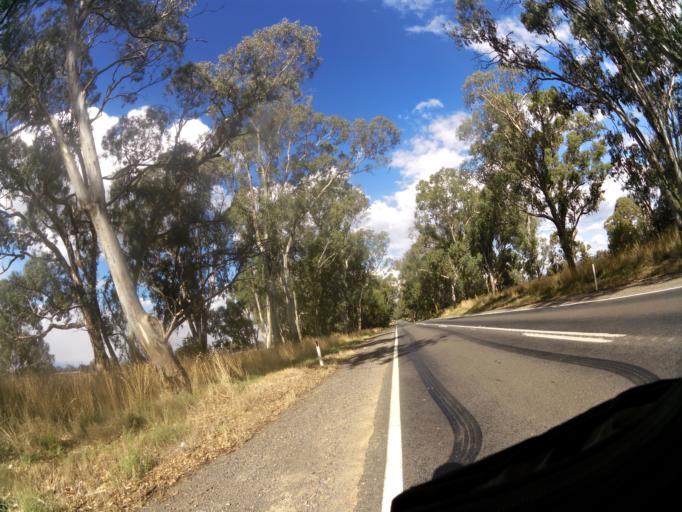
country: AU
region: Victoria
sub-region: Mansfield
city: Mansfield
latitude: -36.9973
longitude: 146.0621
